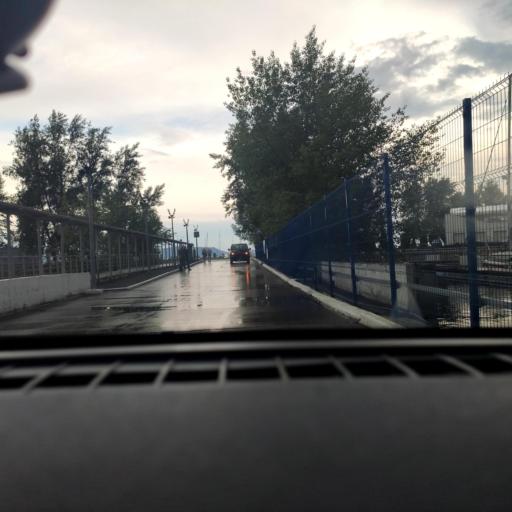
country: RU
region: Samara
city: Tol'yatti
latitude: 53.4688
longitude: 49.3677
